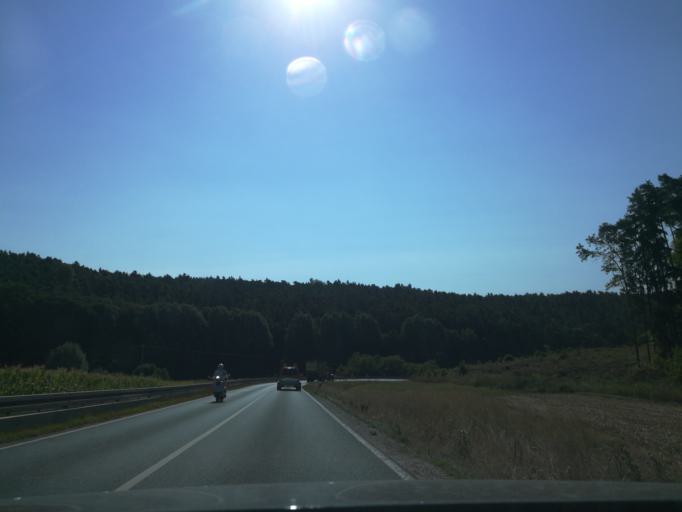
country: DE
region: Bavaria
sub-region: Regierungsbezirk Mittelfranken
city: Ammerndorf
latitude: 49.4364
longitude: 10.8535
